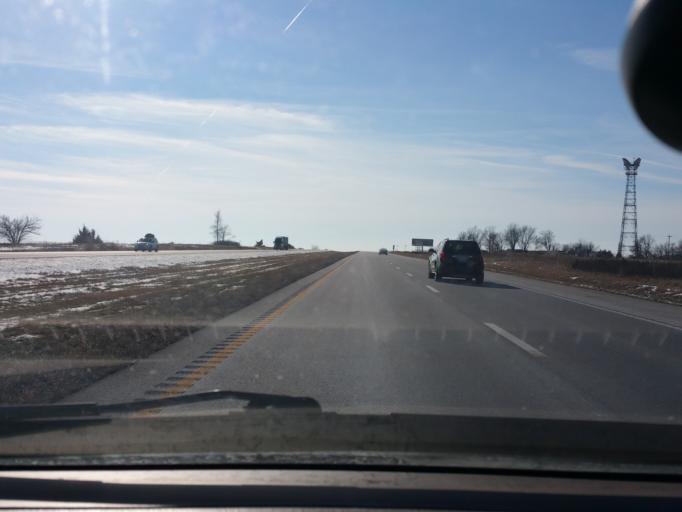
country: US
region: Missouri
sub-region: Clinton County
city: Cameron
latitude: 39.8381
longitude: -94.1838
